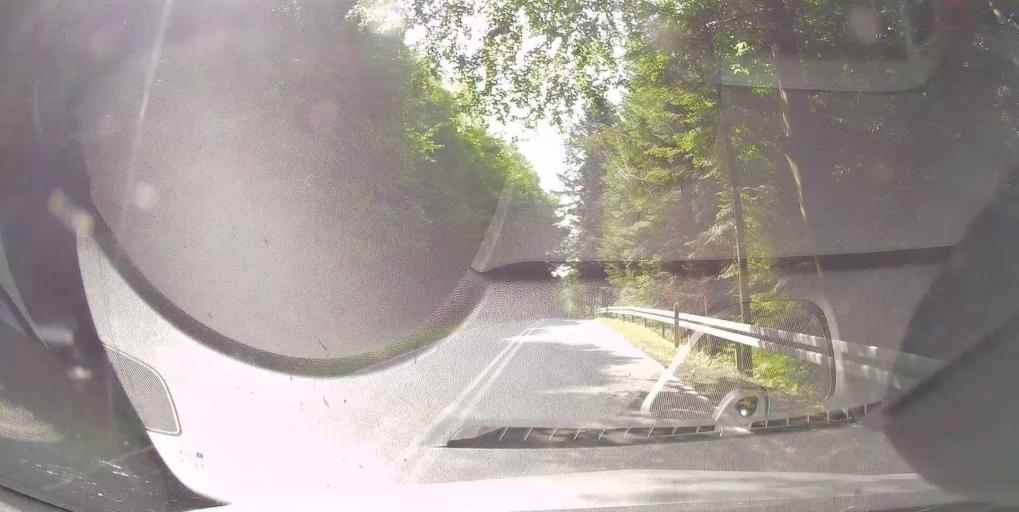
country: PL
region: Lesser Poland Voivodeship
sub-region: Powiat tarnowski
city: Zakliczyn
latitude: 49.7749
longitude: 20.7738
